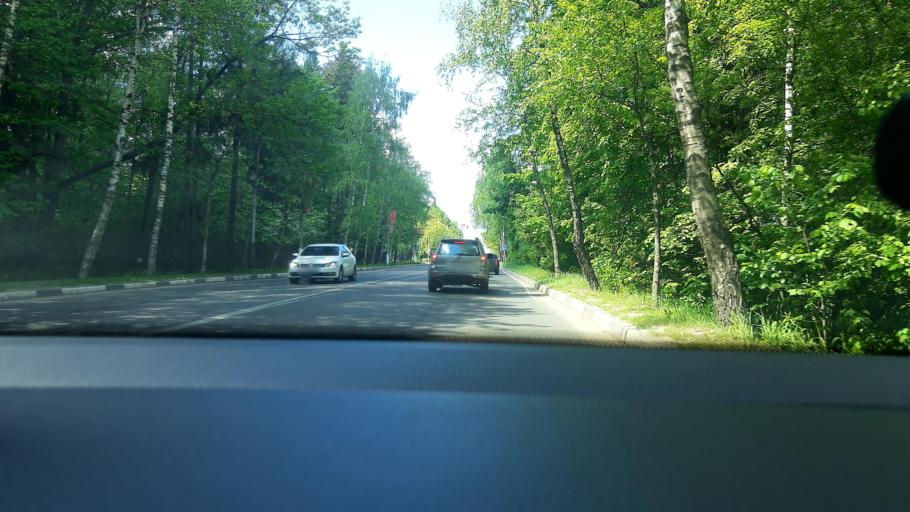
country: RU
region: Moskovskaya
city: Ivanteyevka
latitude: 55.9791
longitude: 37.8988
